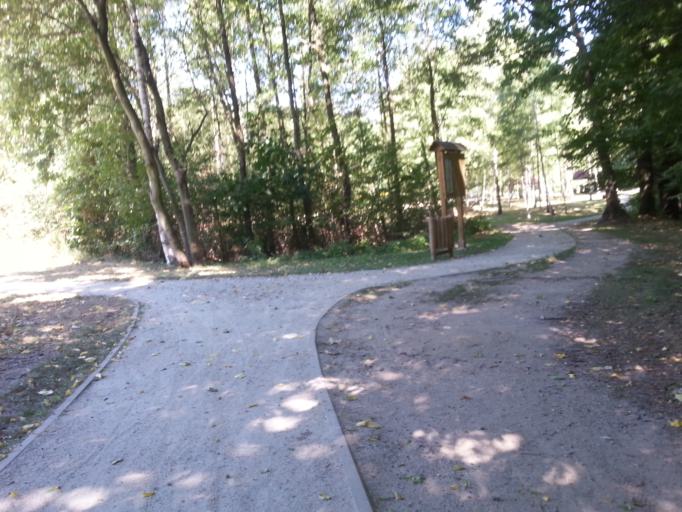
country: PL
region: Lower Silesian Voivodeship
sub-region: Powiat olesnicki
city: Twardogora
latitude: 51.3603
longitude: 17.4622
